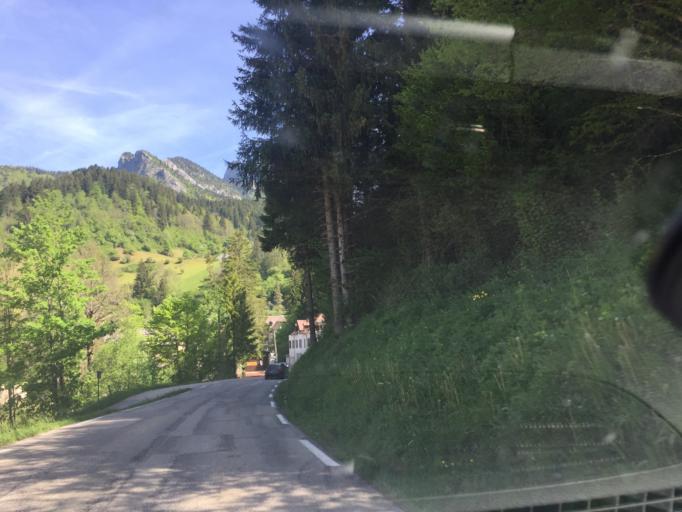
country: FR
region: Rhone-Alpes
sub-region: Departement de l'Isere
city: Le Sappey-en-Chartreuse
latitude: 45.3376
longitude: 5.8071
